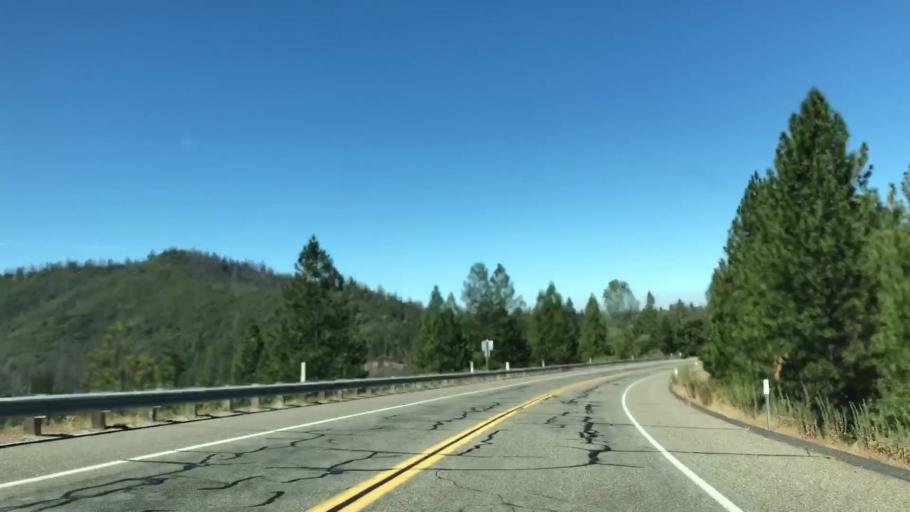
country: US
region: California
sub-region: Tuolumne County
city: Tuolumne City
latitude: 37.8283
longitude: -120.1938
